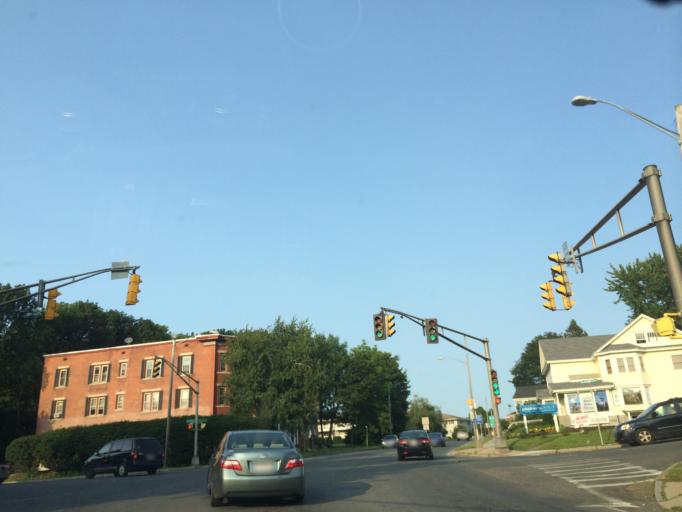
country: US
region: Massachusetts
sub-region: Berkshire County
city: Pittsfield
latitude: 42.4453
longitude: -73.2582
